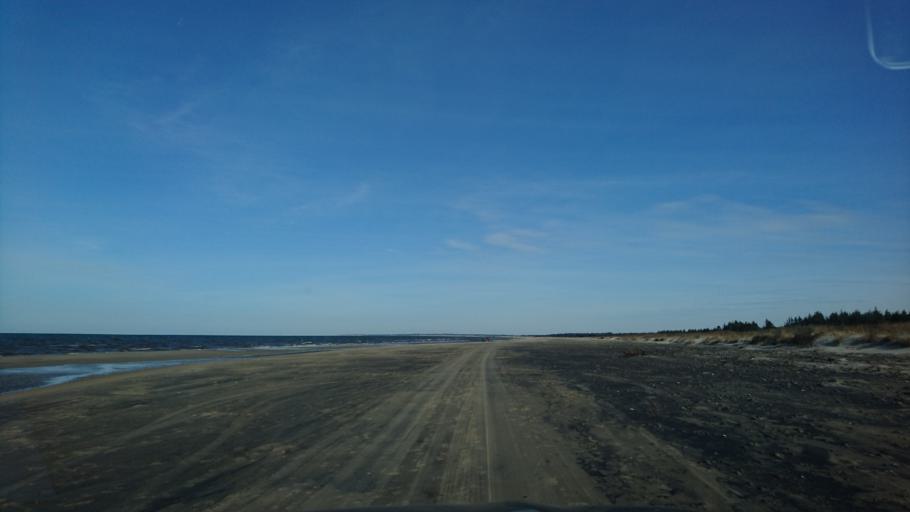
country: DK
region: North Denmark
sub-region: Hjorring Kommune
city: Hirtshals
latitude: 57.5908
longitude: 10.0568
